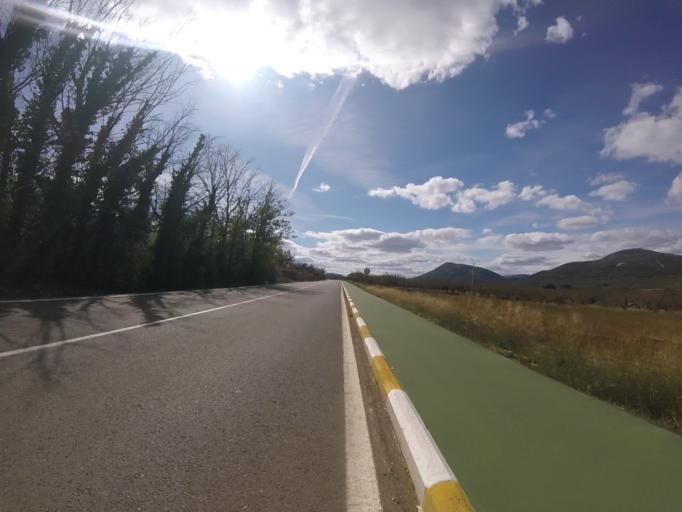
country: ES
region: Valencia
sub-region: Provincia de Castello
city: Cati
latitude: 40.4218
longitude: 0.0744
